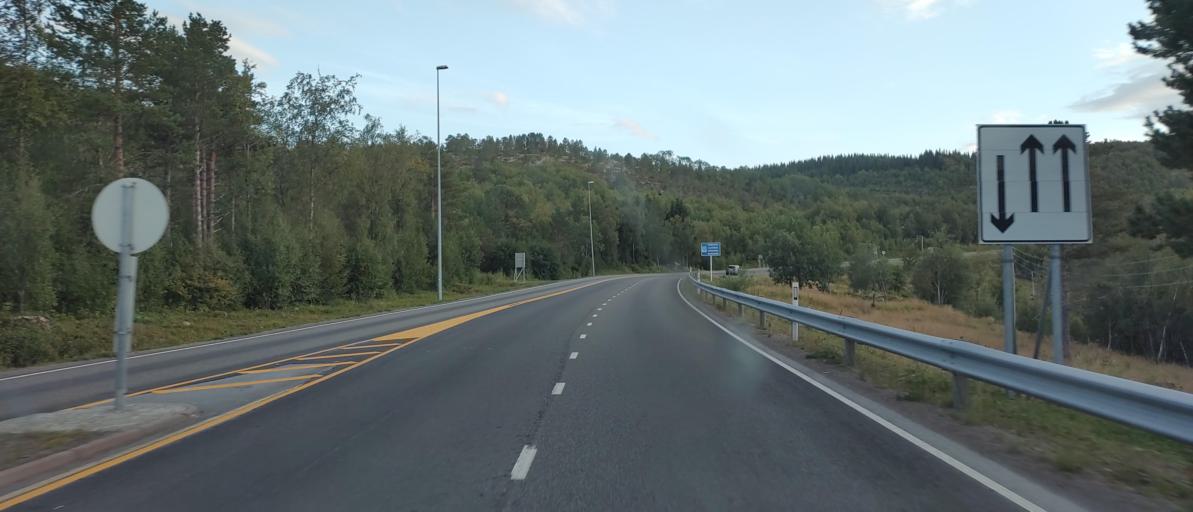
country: NO
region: Nordland
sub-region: Lodingen
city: Lodingen
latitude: 68.2206
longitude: 16.0707
